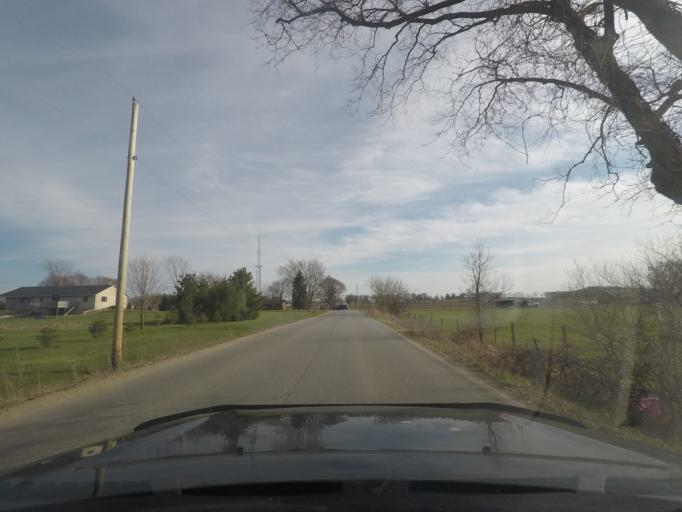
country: US
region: Indiana
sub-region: Elkhart County
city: Dunlap
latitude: 41.5523
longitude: -85.9249
